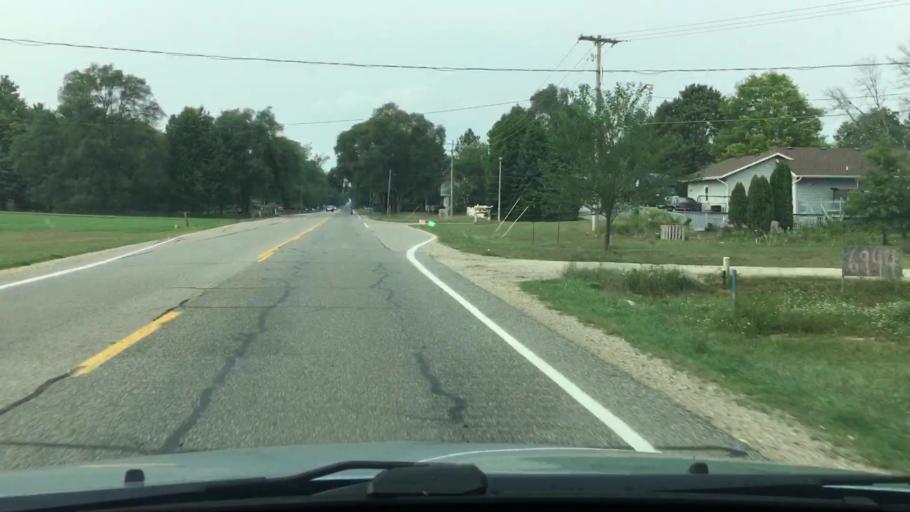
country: US
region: Michigan
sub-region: Ottawa County
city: Hudsonville
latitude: 42.8948
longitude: -85.9017
